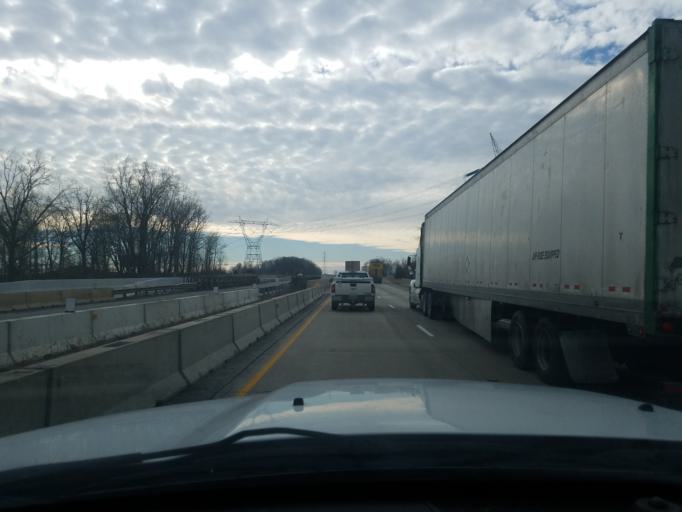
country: US
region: Indiana
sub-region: Huntington County
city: Roanoke
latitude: 40.9190
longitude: -85.3238
